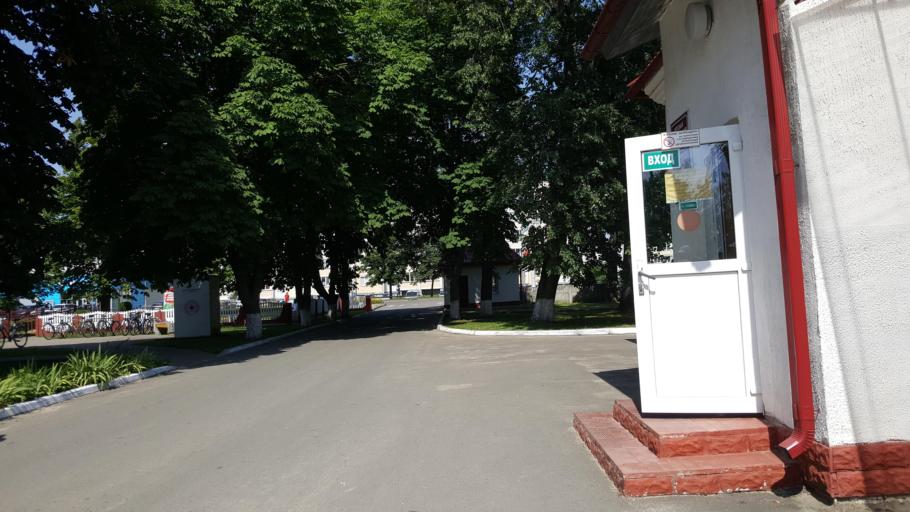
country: BY
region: Brest
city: Zhabinka
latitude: 52.1890
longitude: 24.0304
